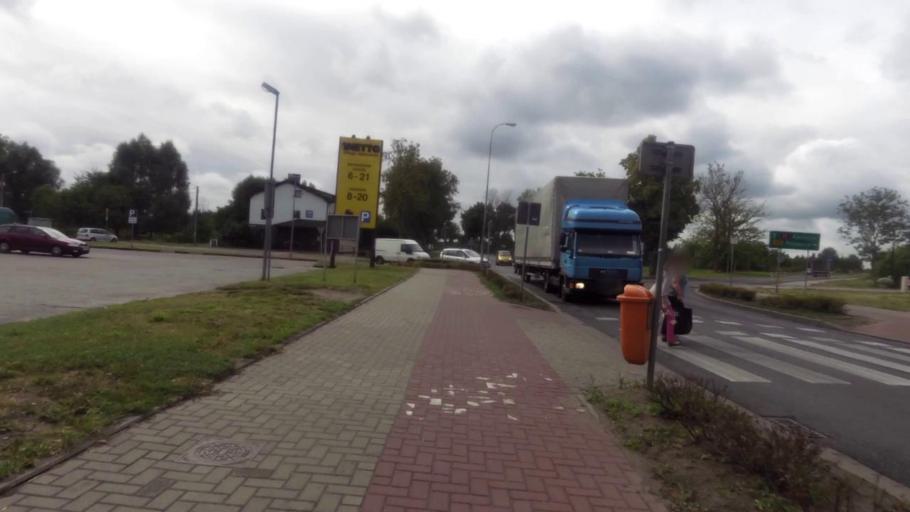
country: PL
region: West Pomeranian Voivodeship
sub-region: Powiat mysliborski
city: Debno
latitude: 52.7329
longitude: 14.6947
